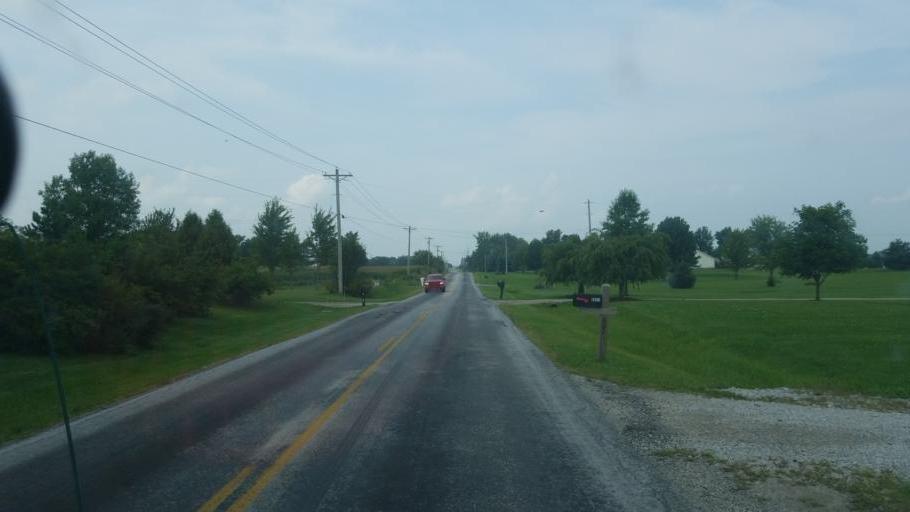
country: US
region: Ohio
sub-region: Lorain County
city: Wellington
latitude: 41.0904
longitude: -82.1614
